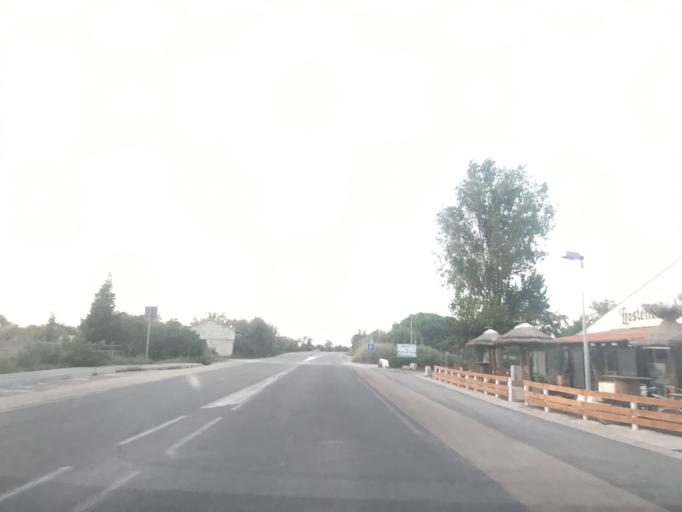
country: FR
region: Provence-Alpes-Cote d'Azur
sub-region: Departement des Bouches-du-Rhone
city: Saintes-Maries-de-la-Mer
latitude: 43.4888
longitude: 4.4039
